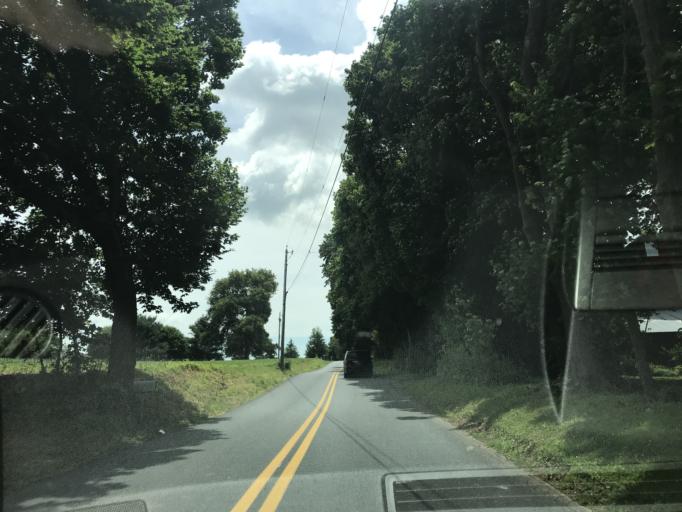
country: US
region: Maryland
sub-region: Carroll County
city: Hampstead
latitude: 39.6289
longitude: -76.7972
